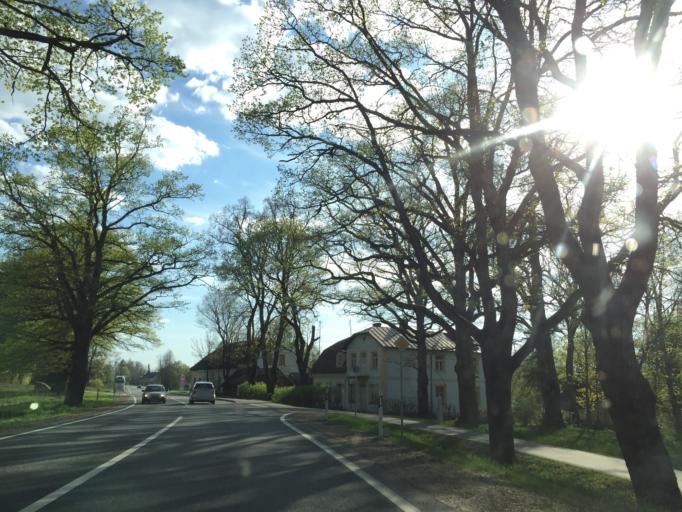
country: LV
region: Pargaujas
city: Stalbe
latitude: 57.3526
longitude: 24.9539
